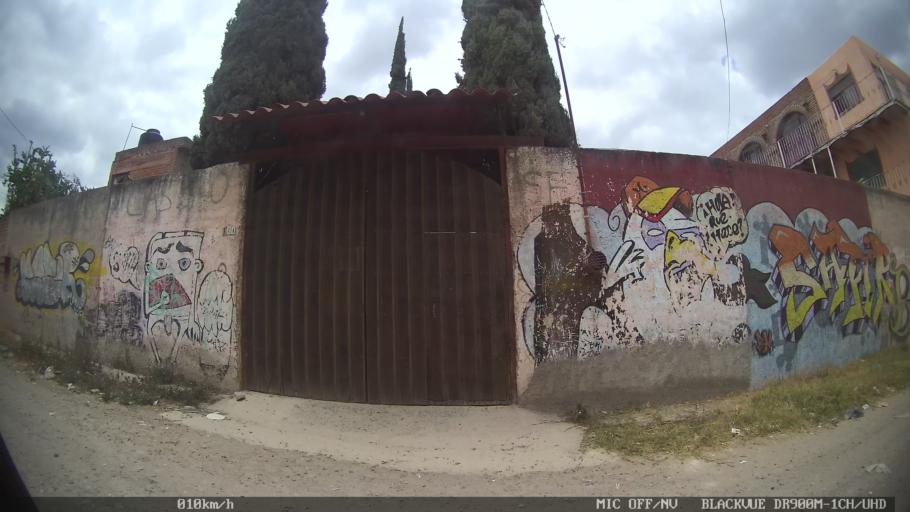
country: MX
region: Jalisco
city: Tonala
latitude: 20.6395
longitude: -103.2614
